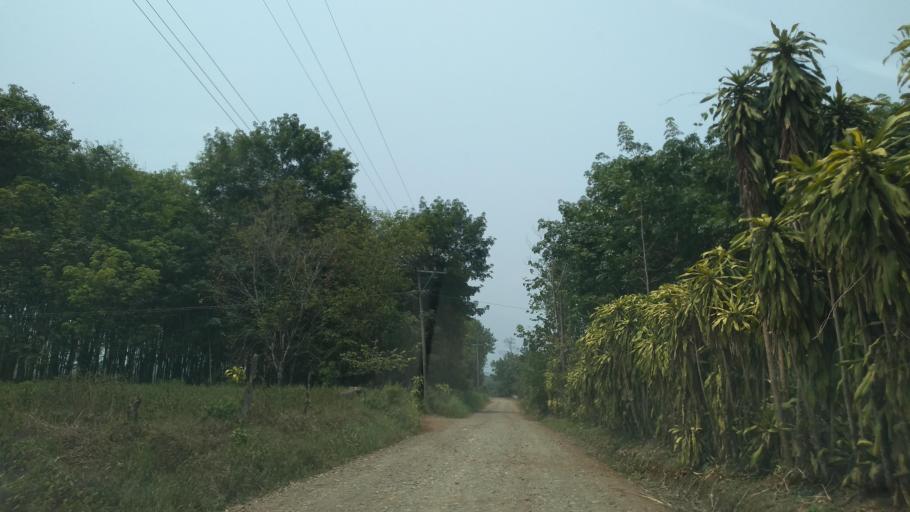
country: MX
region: Veracruz
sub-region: Tezonapa
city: Laguna Chica (Pueblo Nuevo)
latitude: 18.4996
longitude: -96.7746
